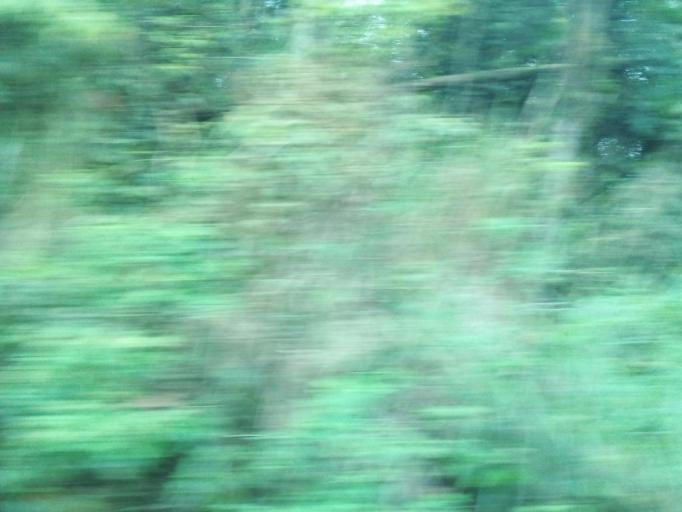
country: BR
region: Minas Gerais
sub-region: Rio Piracicaba
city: Rio Piracicaba
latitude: -19.9711
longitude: -43.2247
